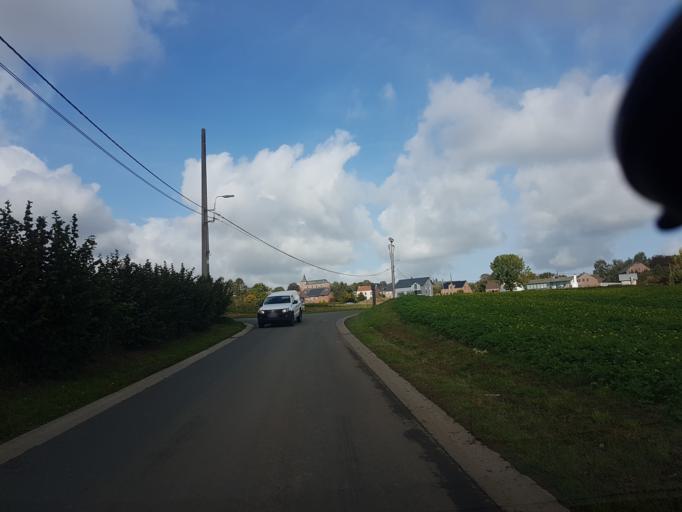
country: BE
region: Wallonia
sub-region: Province de Liege
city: Heron
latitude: 50.5472
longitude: 5.1025
